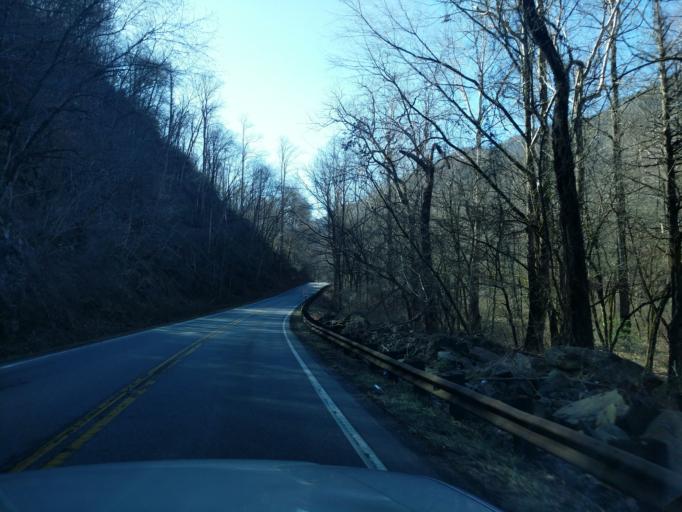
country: US
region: North Carolina
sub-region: Graham County
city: Robbinsville
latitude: 35.3073
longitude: -83.6462
